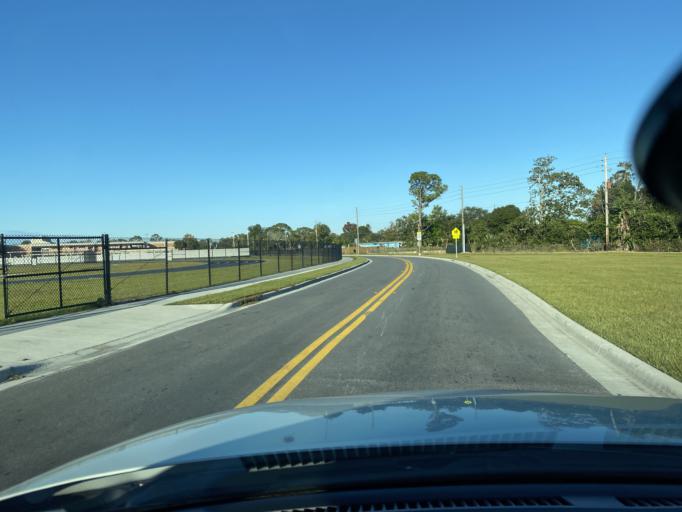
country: US
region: Florida
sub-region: Orange County
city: Azalea Park
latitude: 28.5314
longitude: -81.3004
